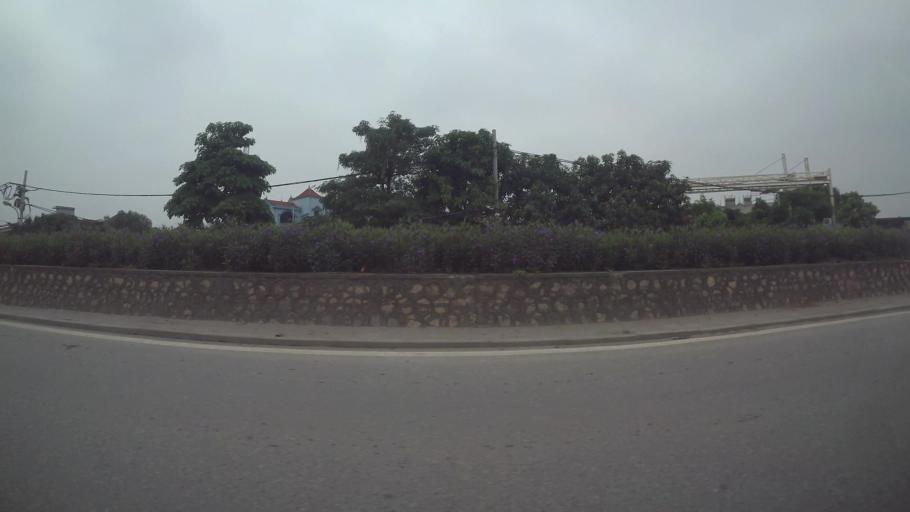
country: VN
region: Ha Noi
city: Hai BaTrung
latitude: 20.9905
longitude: 105.8933
